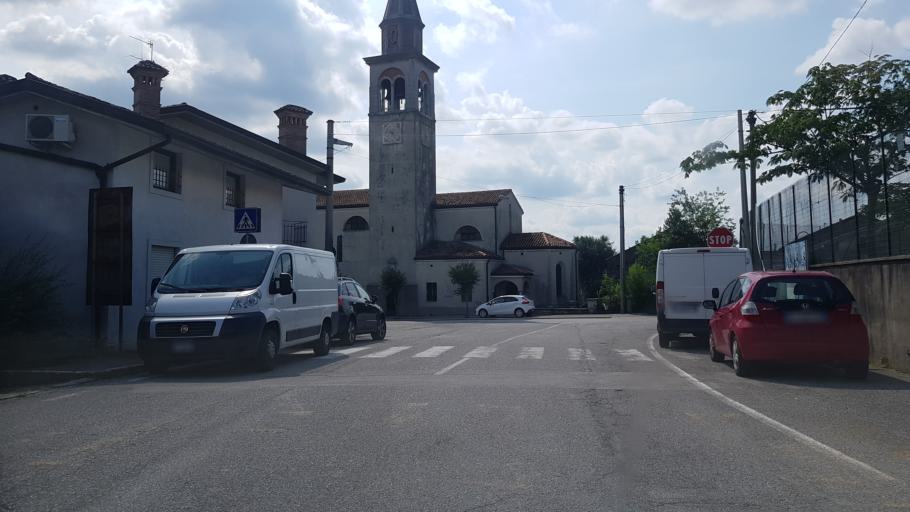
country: IT
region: Friuli Venezia Giulia
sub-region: Provincia di Gorizia
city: Savogna d'Isonzo
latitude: 45.9027
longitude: 13.5729
